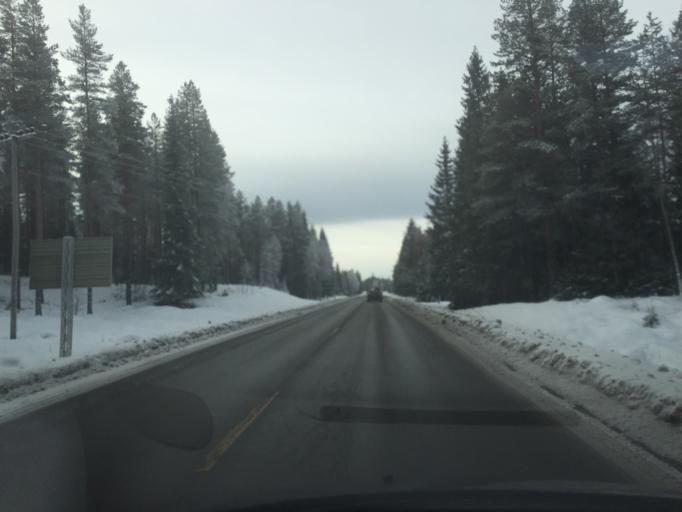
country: NO
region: Hedmark
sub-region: Elverum
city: Elverum
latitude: 60.9812
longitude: 11.7468
